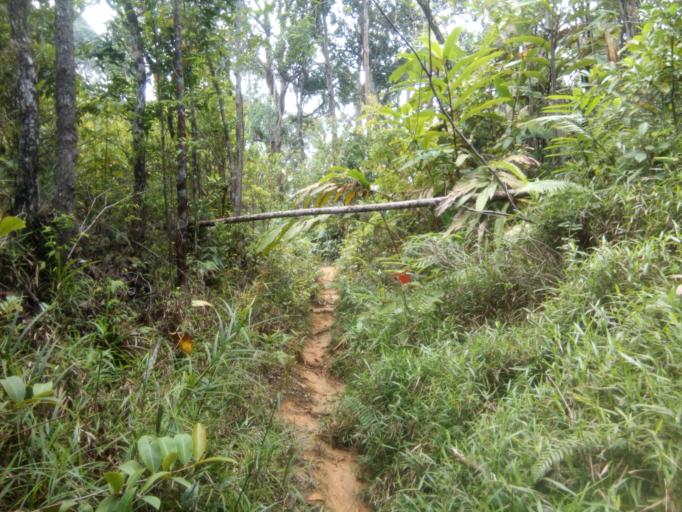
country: MY
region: Penang
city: Tanjung Tokong
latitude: 5.4273
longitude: 100.2821
